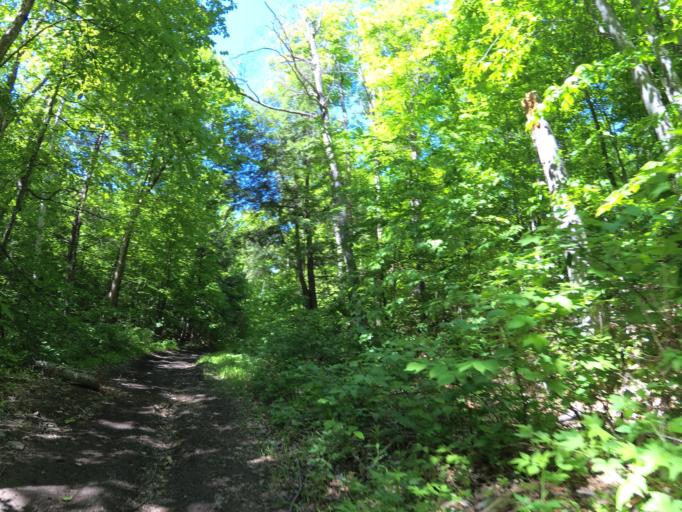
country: CA
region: Ontario
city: Renfrew
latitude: 45.0569
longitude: -77.0848
